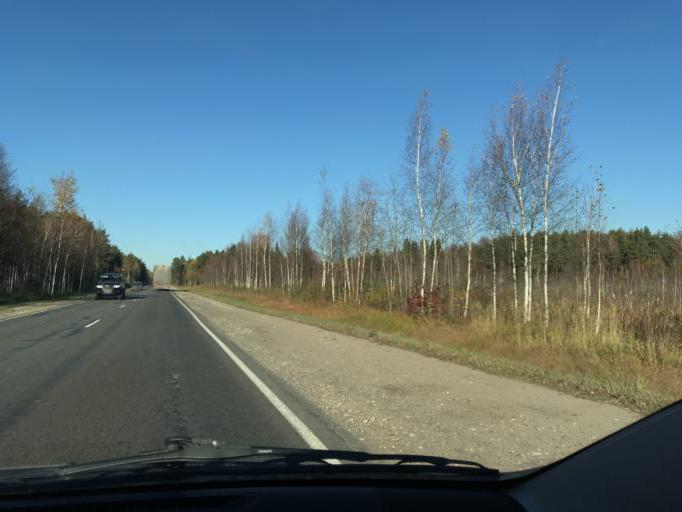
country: BY
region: Vitebsk
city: Polatsk
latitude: 55.5089
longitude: 28.7444
